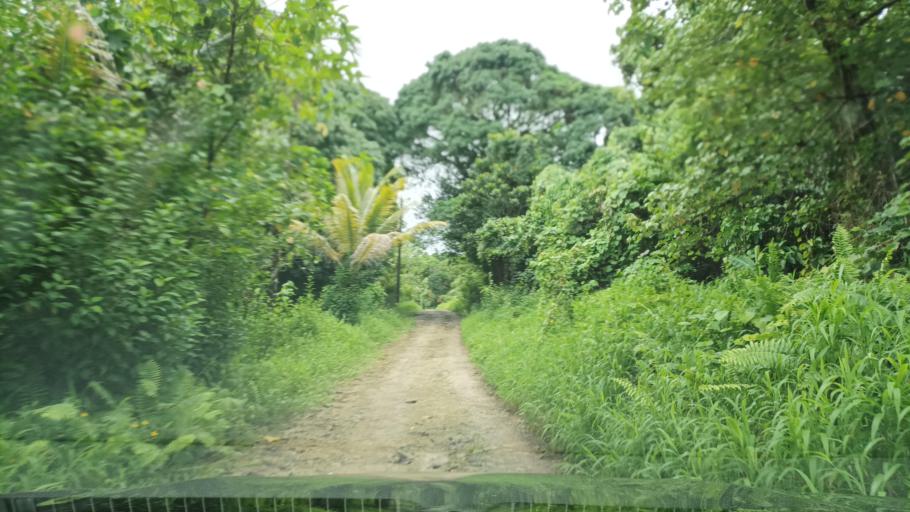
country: FM
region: Pohnpei
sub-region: Madolenihm Municipality
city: Madolenihm Municipality Government
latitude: 6.8185
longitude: 158.2843
